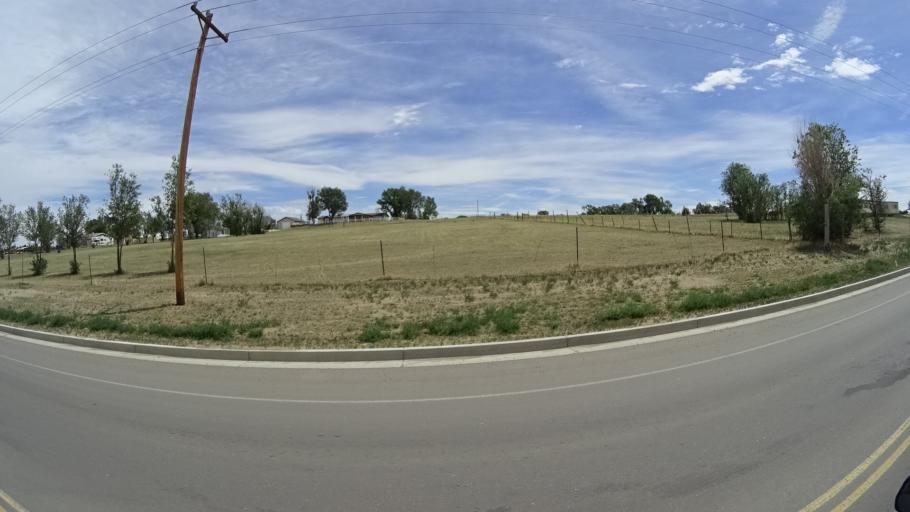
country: US
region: Colorado
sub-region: El Paso County
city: Fountain
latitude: 38.6950
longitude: -104.6736
